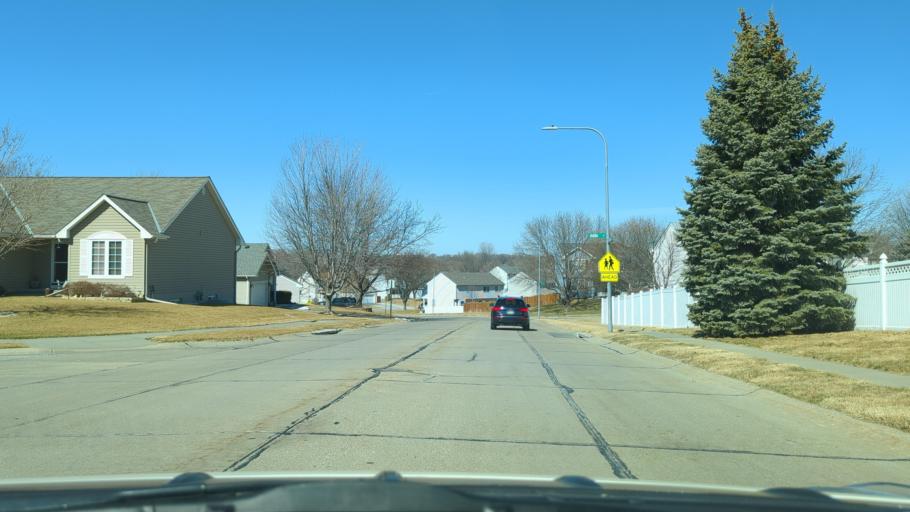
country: US
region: Nebraska
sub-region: Douglas County
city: Ralston
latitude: 41.1805
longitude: -96.0646
